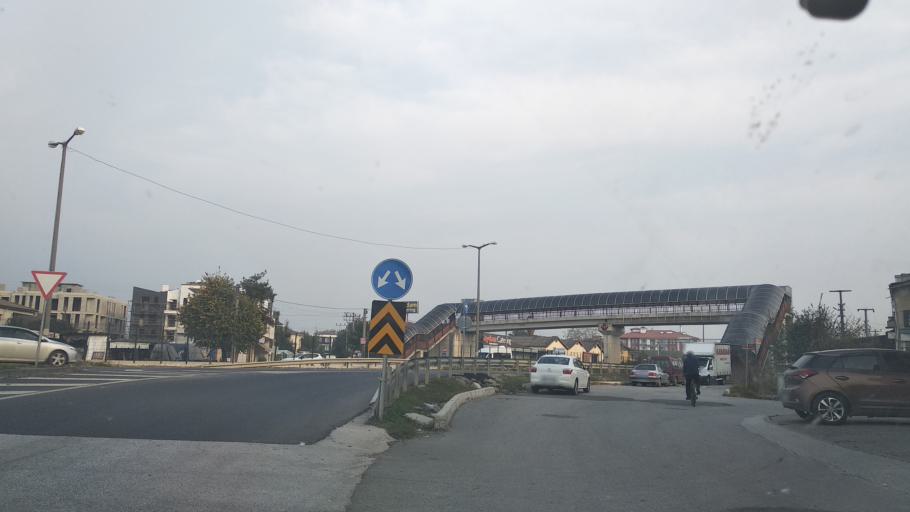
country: TR
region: Duzce
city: Duzce
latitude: 40.8360
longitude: 31.1747
